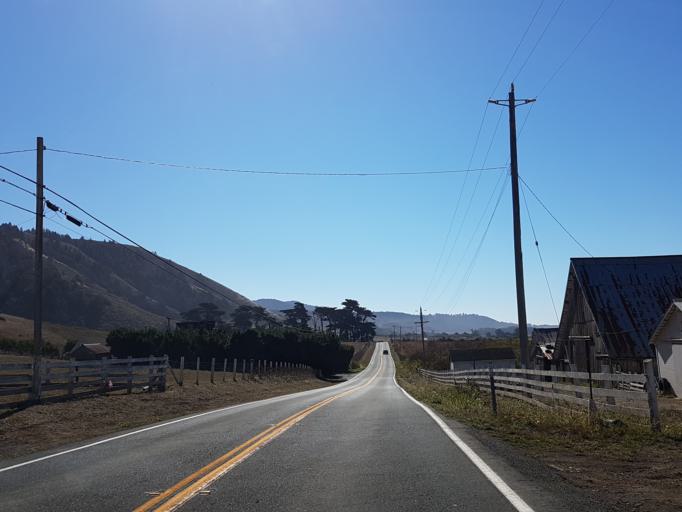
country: US
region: California
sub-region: Mendocino County
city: Boonville
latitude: 39.0808
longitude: -123.6966
